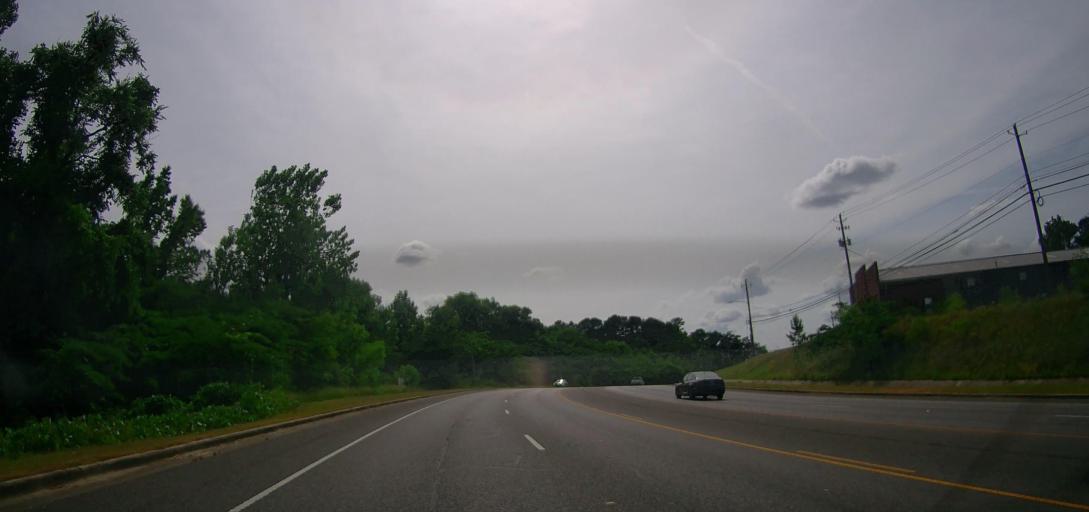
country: US
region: Alabama
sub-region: Jefferson County
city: Irondale
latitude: 33.5308
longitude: -86.6874
